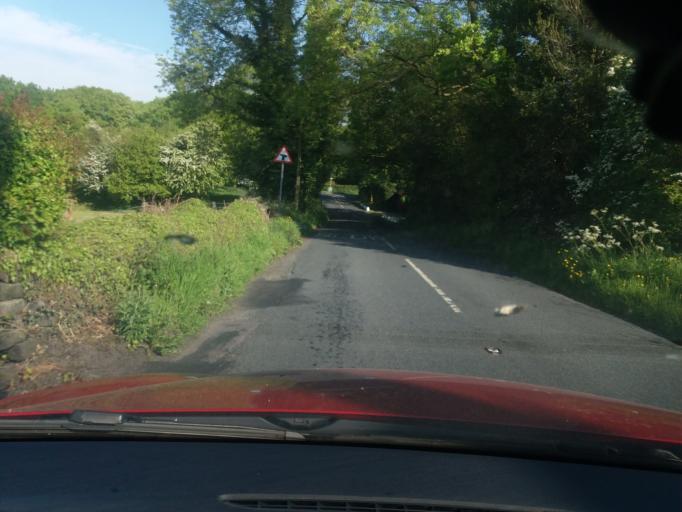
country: GB
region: England
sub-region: Borough of Wigan
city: Haigh
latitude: 53.6117
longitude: -2.5763
